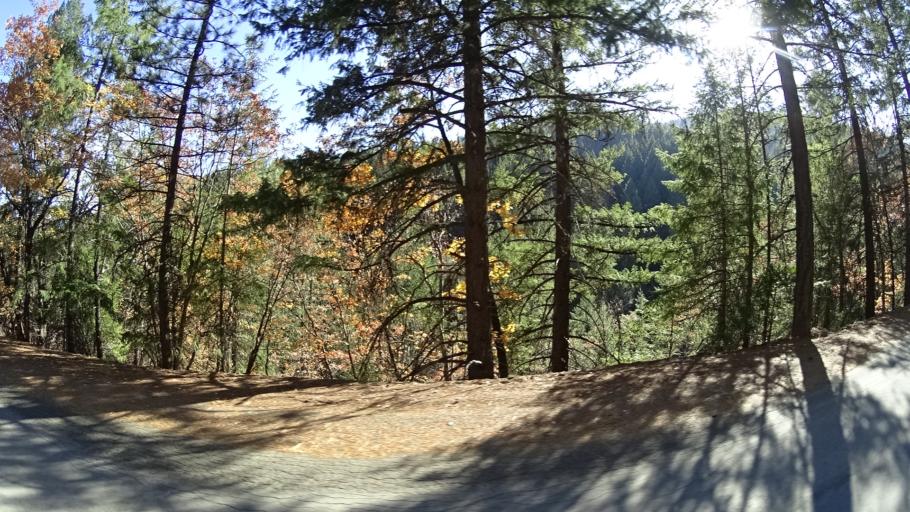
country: US
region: California
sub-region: Siskiyou County
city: Yreka
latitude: 41.7286
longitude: -122.7116
